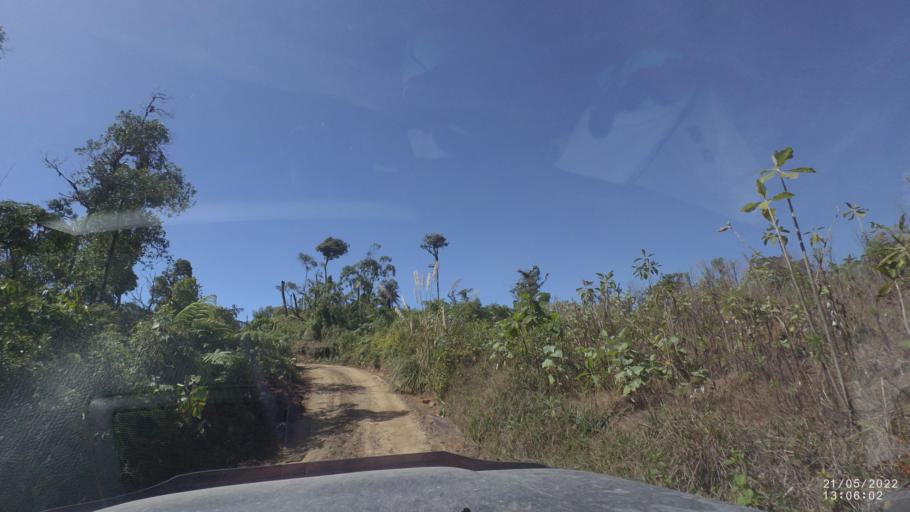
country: BO
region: Cochabamba
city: Colomi
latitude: -17.1542
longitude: -65.9478
